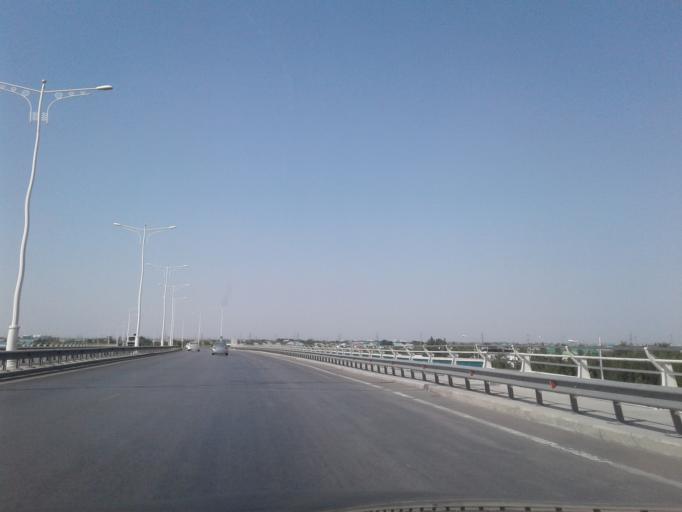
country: TM
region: Ahal
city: Ashgabat
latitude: 37.9634
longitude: 58.4212
